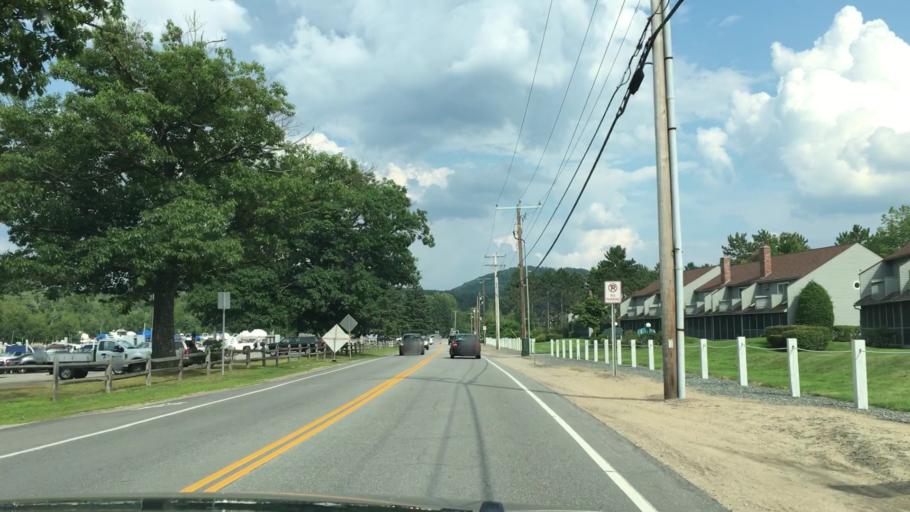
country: US
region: New Hampshire
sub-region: Belknap County
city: Gilford
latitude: 43.5792
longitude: -71.4071
